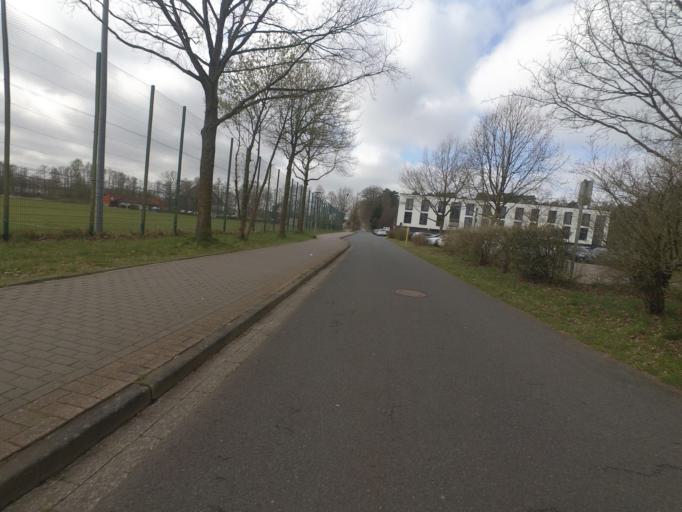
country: DE
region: Lower Saxony
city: Oldenburg
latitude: 53.1636
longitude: 8.1753
